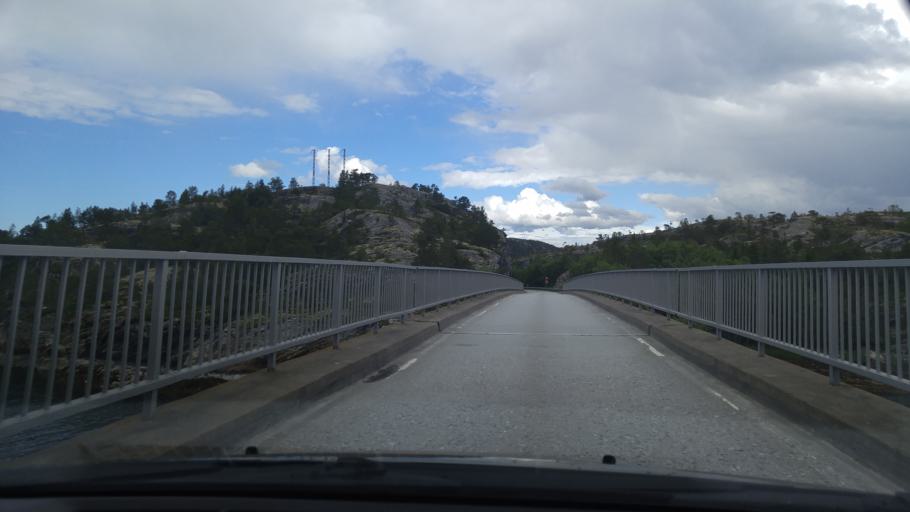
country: NO
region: Nord-Trondelag
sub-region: Naeroy
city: Kolvereid
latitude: 64.7499
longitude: 11.5671
